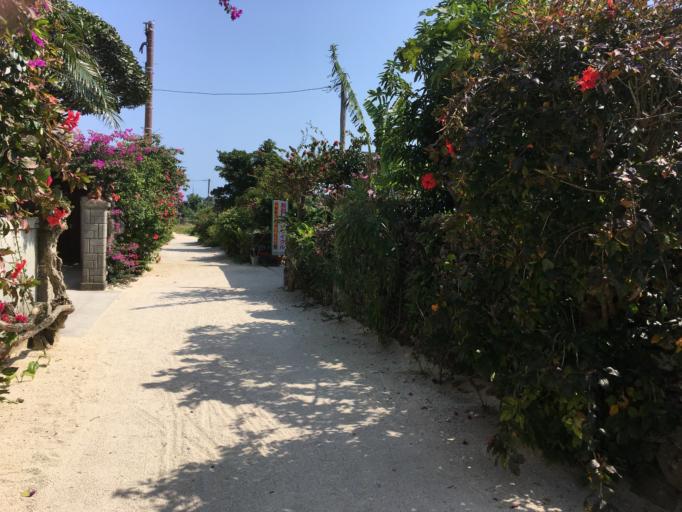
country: JP
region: Okinawa
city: Ishigaki
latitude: 24.3292
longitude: 124.0874
